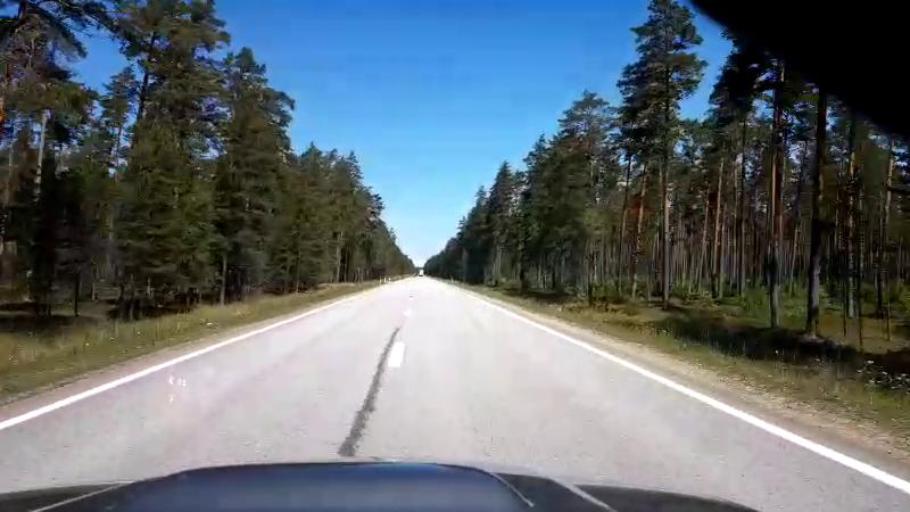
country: LV
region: Salacgrivas
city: Salacgriva
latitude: 57.5524
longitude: 24.4331
